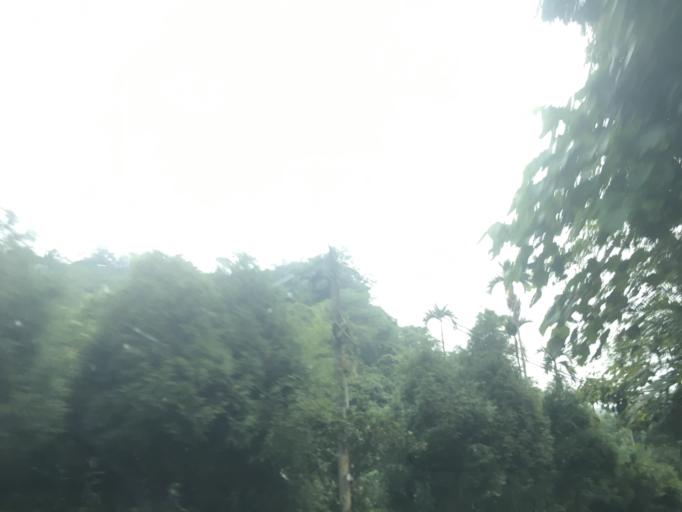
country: TW
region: Taiwan
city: Fengyuan
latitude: 24.1906
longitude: 120.7695
